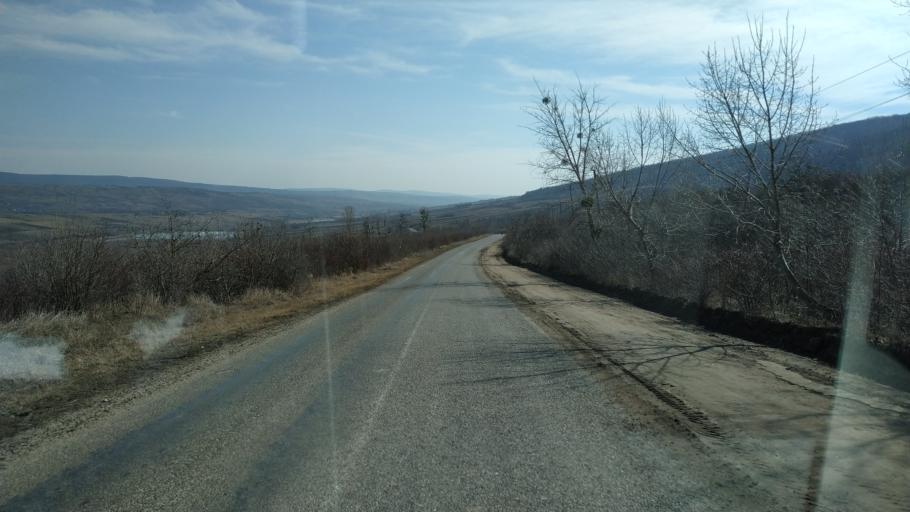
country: MD
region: Nisporeni
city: Nisporeni
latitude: 47.1885
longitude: 28.0701
